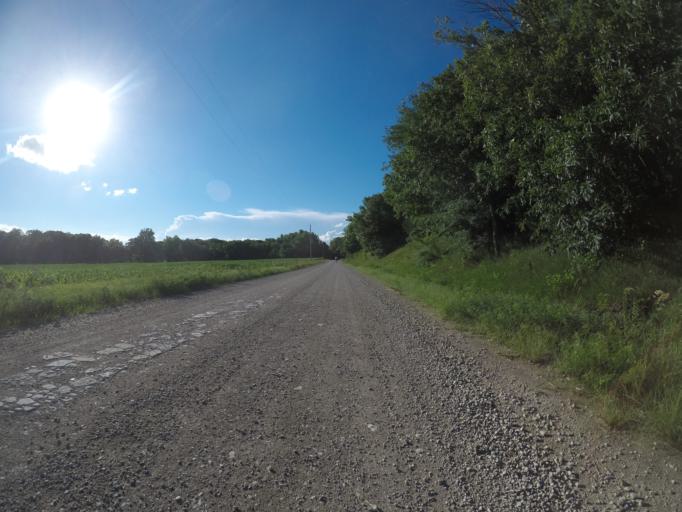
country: US
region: Kansas
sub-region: Riley County
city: Ogden
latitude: 39.2452
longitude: -96.7345
